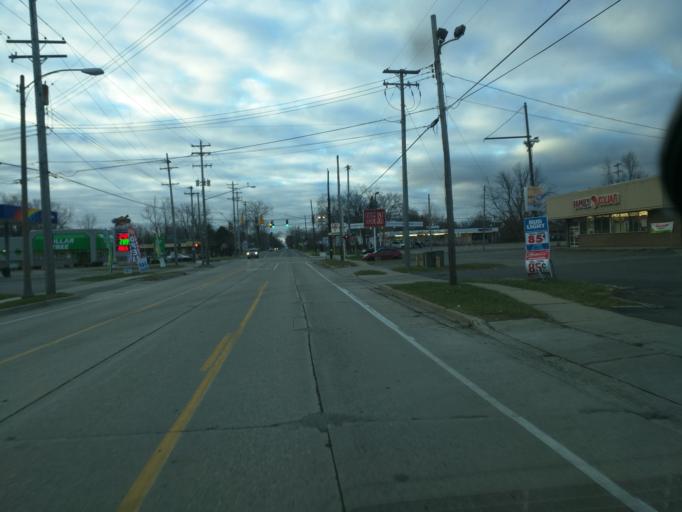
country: US
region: Michigan
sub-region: Eaton County
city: Waverly
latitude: 42.6839
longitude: -84.6031
